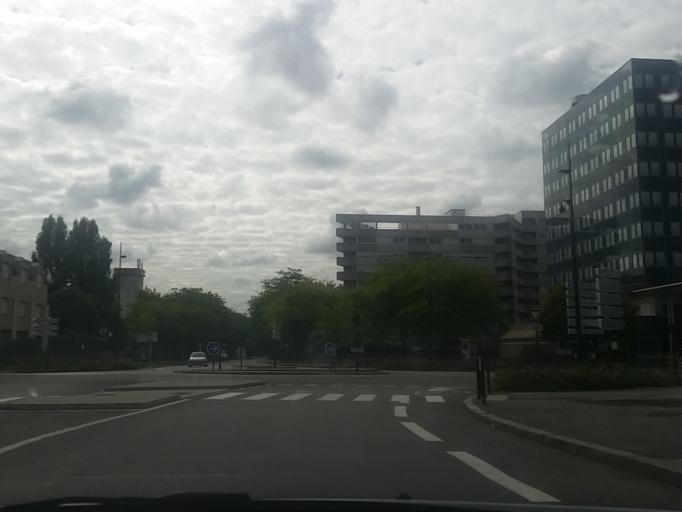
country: FR
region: Pays de la Loire
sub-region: Departement de la Loire-Atlantique
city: Nantes
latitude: 47.2083
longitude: -1.5305
